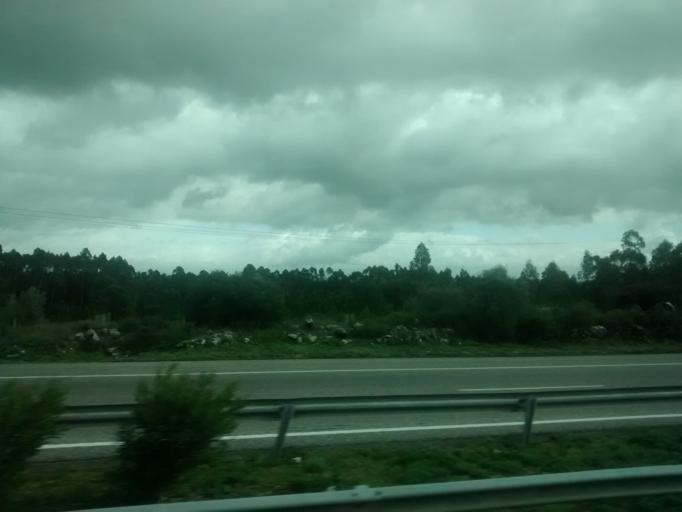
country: PT
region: Santarem
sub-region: Ourem
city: Fatima
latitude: 39.5979
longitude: -8.6697
